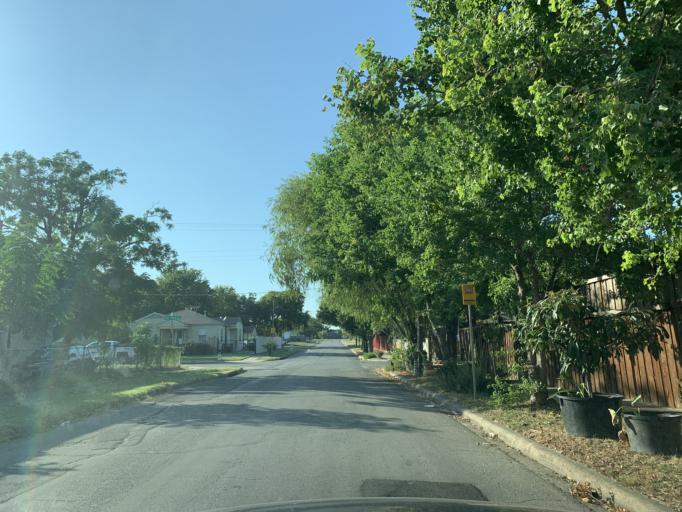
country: US
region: Texas
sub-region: Dallas County
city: Dallas
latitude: 32.7075
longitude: -96.7943
